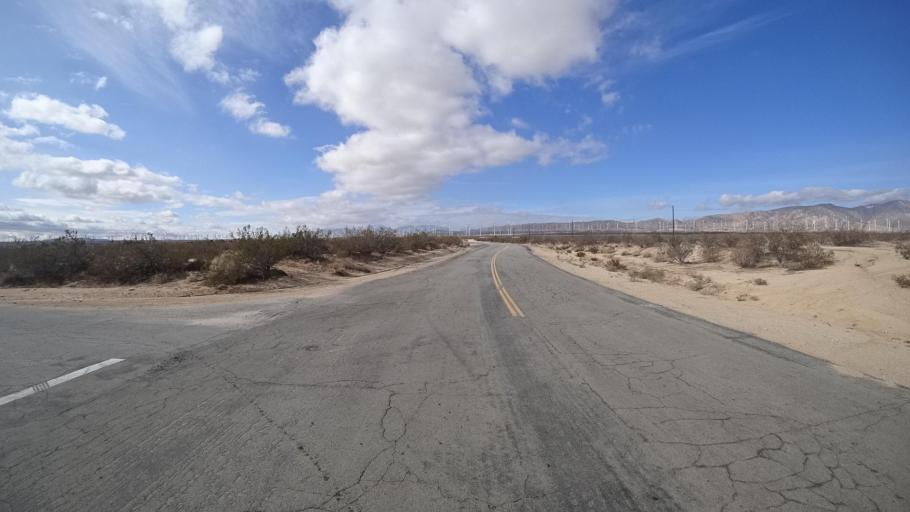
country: US
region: California
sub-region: Kern County
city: Mojave
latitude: 35.0685
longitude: -118.1837
